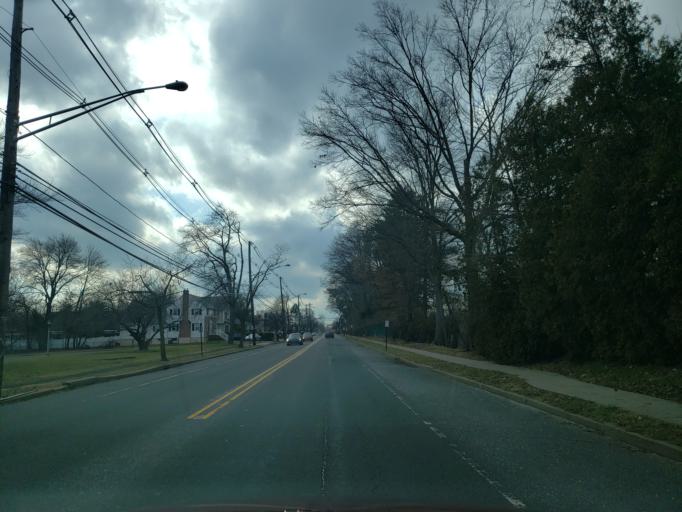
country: US
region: New Jersey
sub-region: Union County
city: Springfield
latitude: 40.6941
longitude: -74.3281
